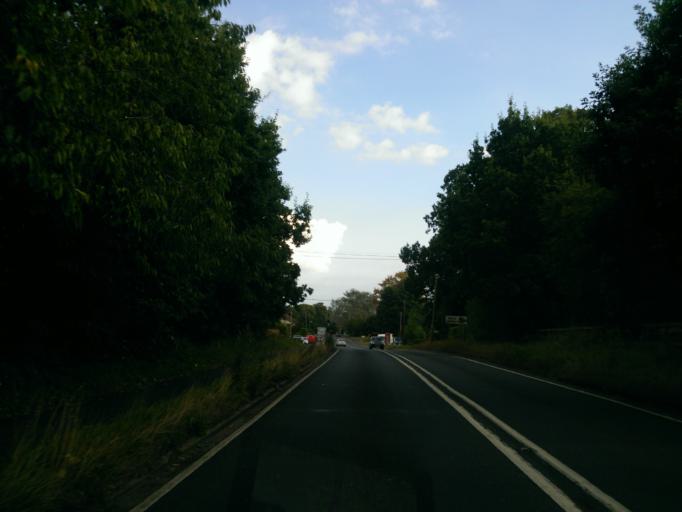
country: GB
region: England
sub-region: Essex
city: Sible Hedingham
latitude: 51.9852
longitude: 0.5872
